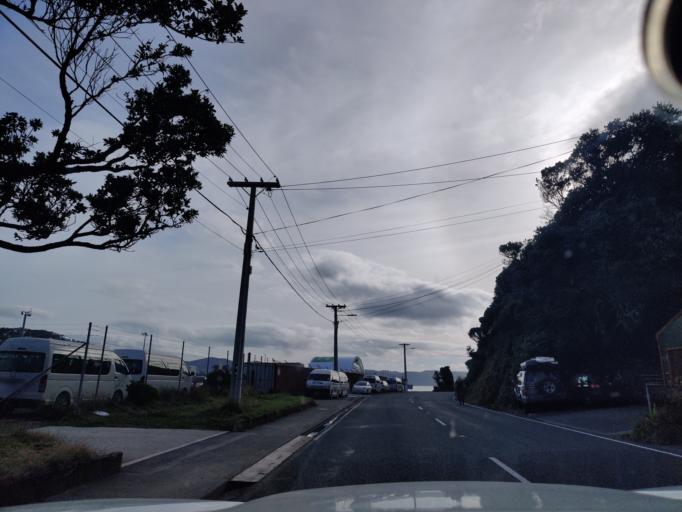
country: NZ
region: Wellington
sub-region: Wellington City
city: Wellington
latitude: -41.3115
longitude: 174.8124
